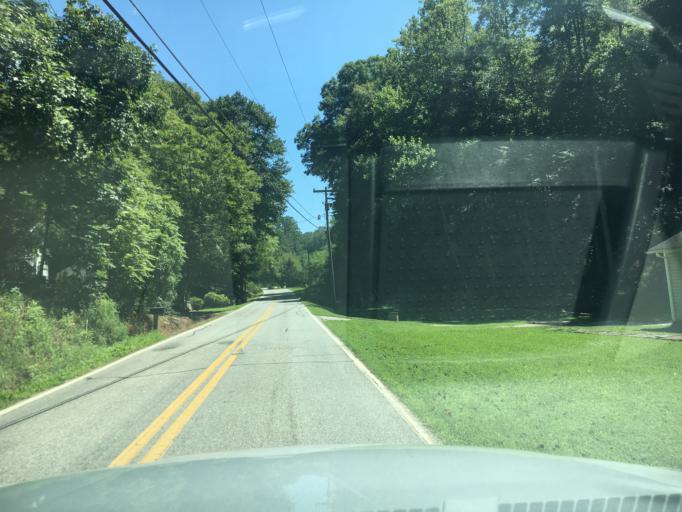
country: US
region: North Carolina
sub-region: McDowell County
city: Marion
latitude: 35.6927
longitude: -82.0402
